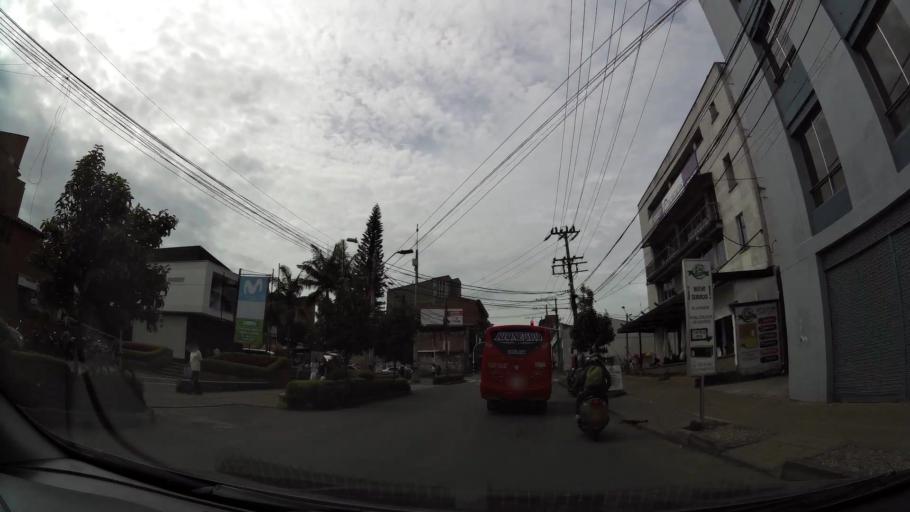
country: CO
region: Antioquia
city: Rionegro
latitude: 6.1508
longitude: -75.3731
